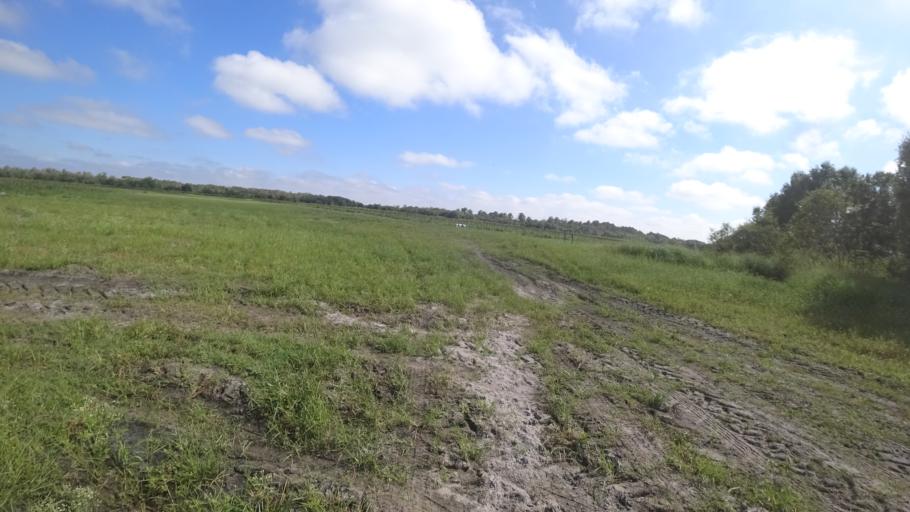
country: US
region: Florida
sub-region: DeSoto County
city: Arcadia
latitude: 27.2792
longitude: -82.0816
